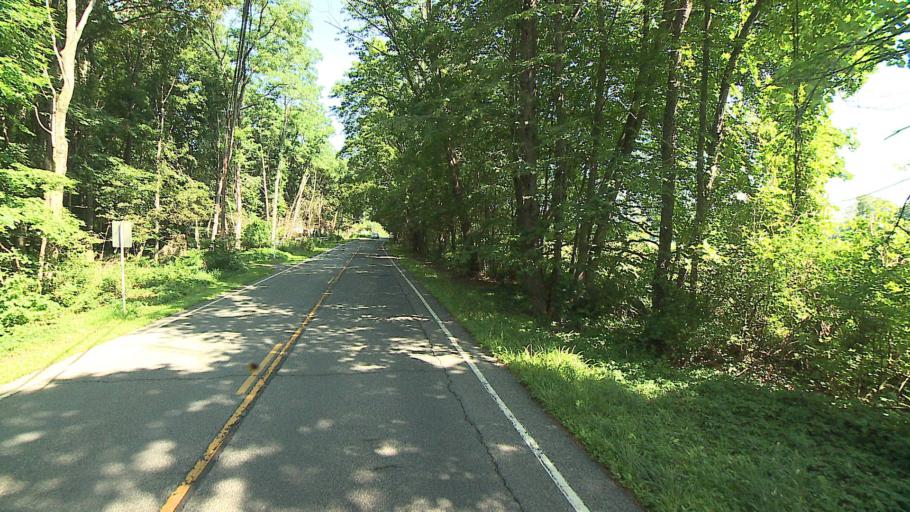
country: US
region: Connecticut
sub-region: Litchfield County
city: Canaan
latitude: 42.0180
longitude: -73.4301
